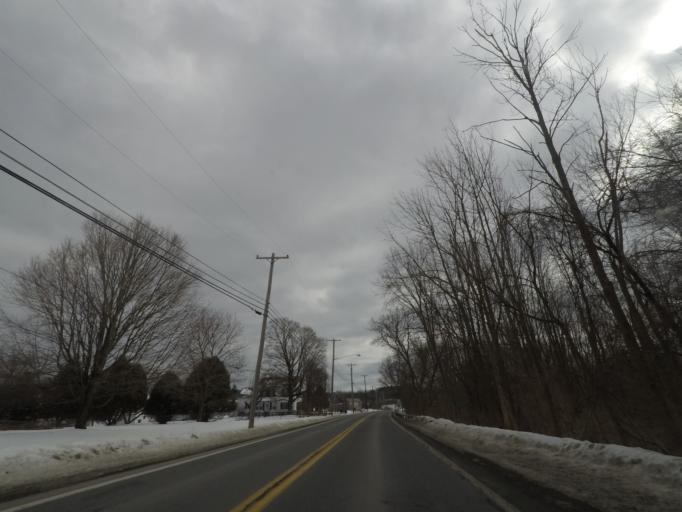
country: US
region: New York
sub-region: Washington County
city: Greenwich
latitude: 43.0841
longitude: -73.4875
